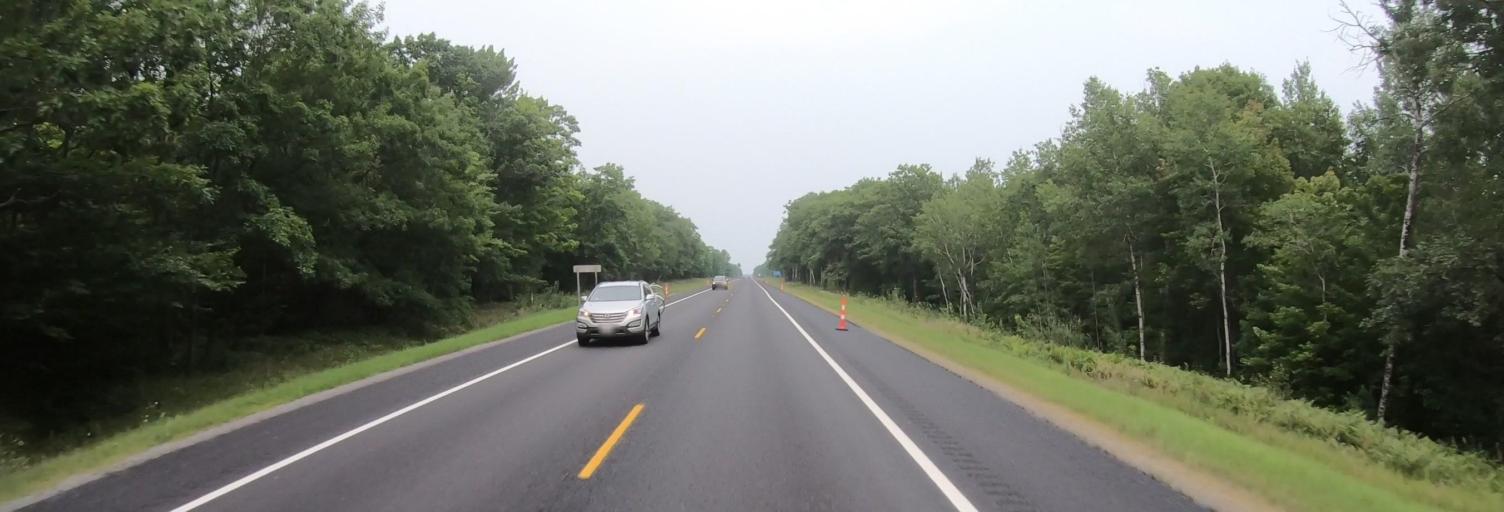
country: US
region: Michigan
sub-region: Mackinac County
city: Saint Ignace
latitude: 45.7046
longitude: -84.7685
